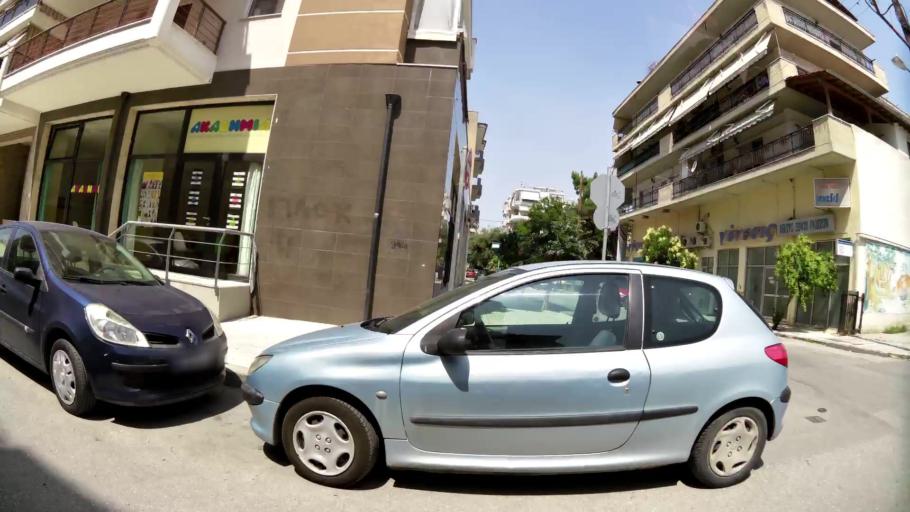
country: GR
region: Central Macedonia
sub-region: Nomos Thessalonikis
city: Evosmos
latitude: 40.6725
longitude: 22.9098
